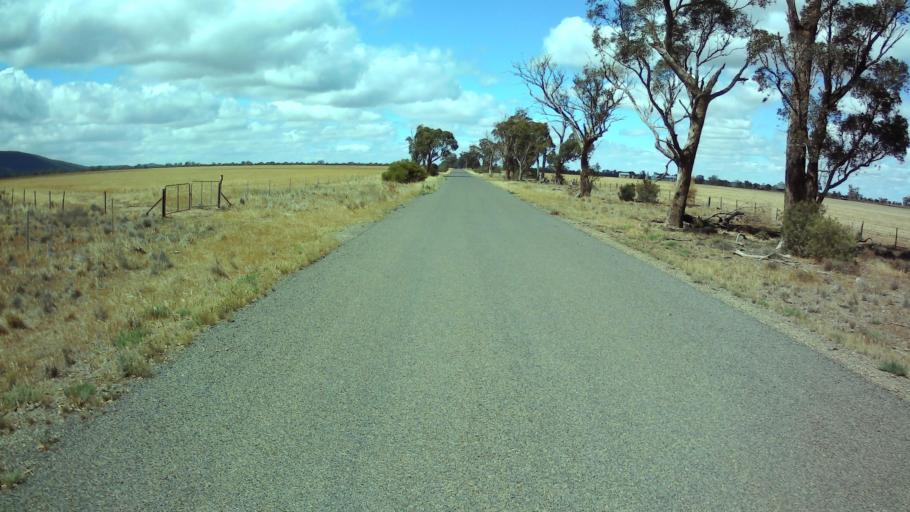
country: AU
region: New South Wales
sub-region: Weddin
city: Grenfell
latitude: -33.8758
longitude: 147.9251
